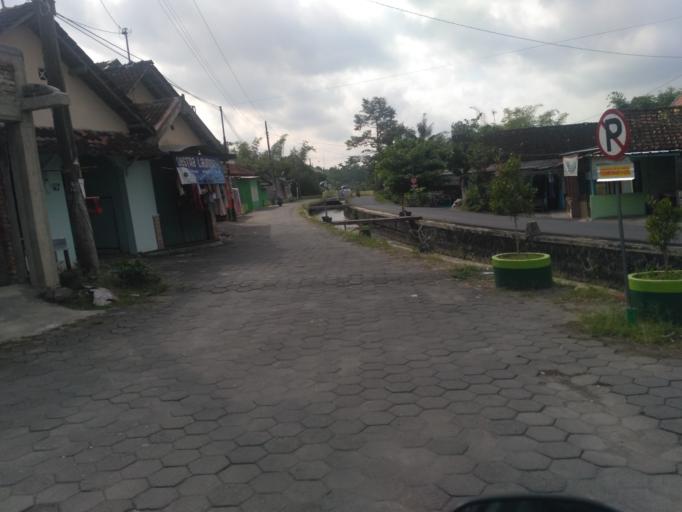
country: ID
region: Daerah Istimewa Yogyakarta
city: Melati
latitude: -7.7526
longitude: 110.3513
